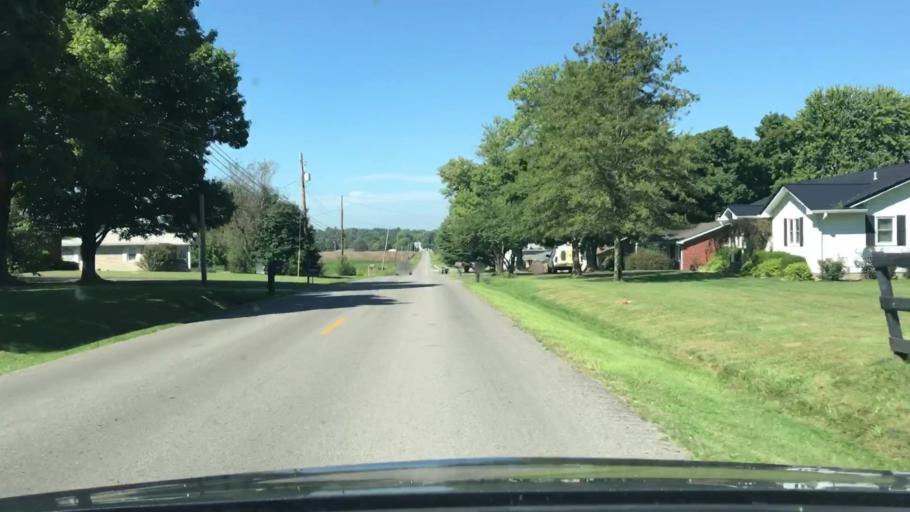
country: US
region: Kentucky
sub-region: Hardin County
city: Elizabethtown
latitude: 37.6019
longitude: -85.8919
